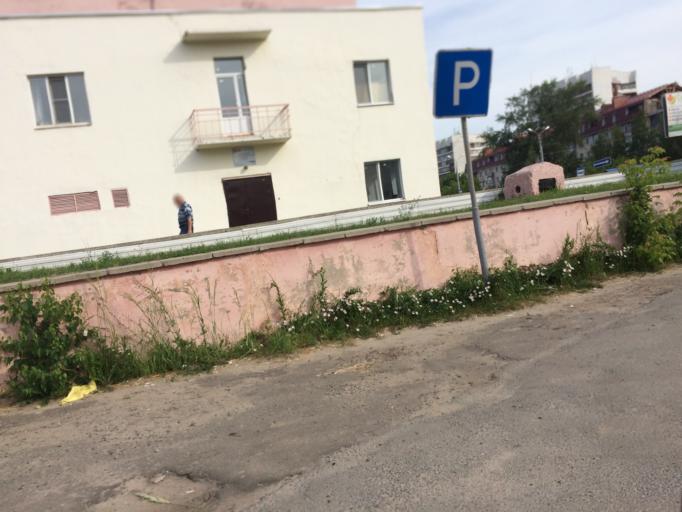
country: RU
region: Mariy-El
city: Yoshkar-Ola
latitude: 56.6204
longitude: 47.8823
